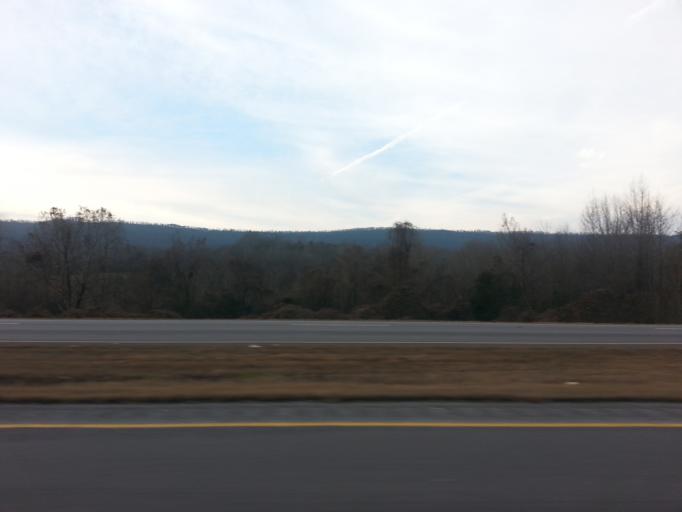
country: US
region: Tennessee
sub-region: Rhea County
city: Spring City
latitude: 35.6578
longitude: -84.8815
